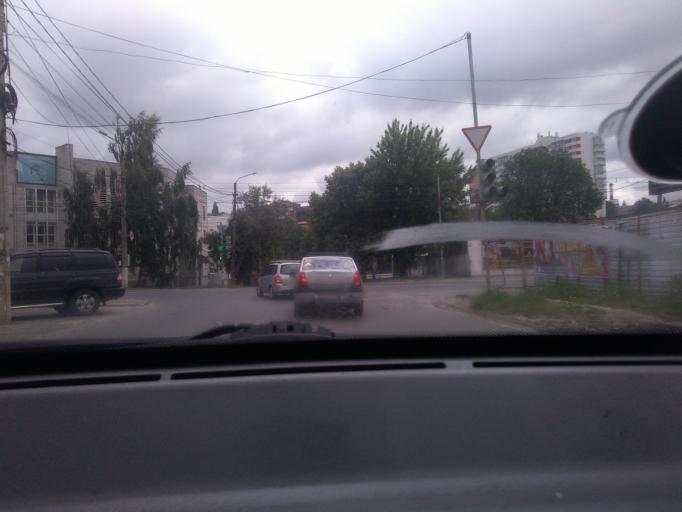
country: RU
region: Kursk
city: Kursk
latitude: 51.7312
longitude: 36.1802
